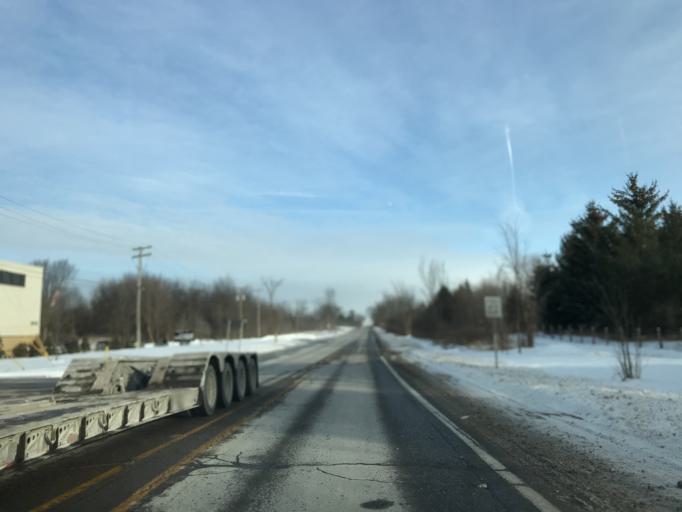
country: US
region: Michigan
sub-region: Oakland County
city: Wixom
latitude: 42.5232
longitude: -83.5755
